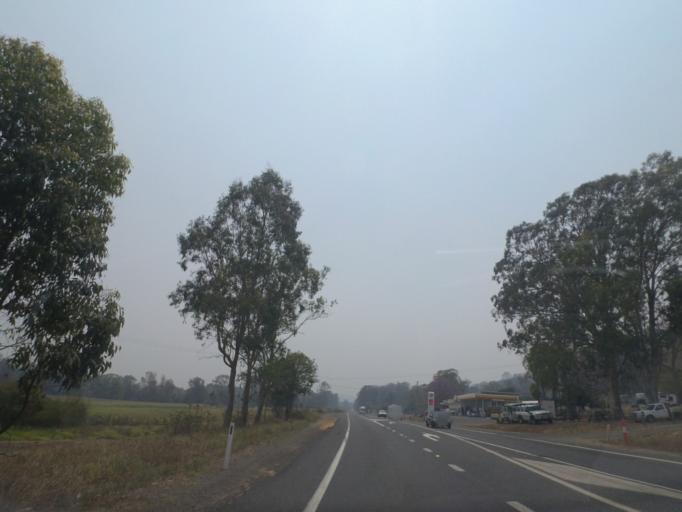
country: AU
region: New South Wales
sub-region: Clarence Valley
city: Maclean
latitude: -29.5618
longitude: 153.1485
